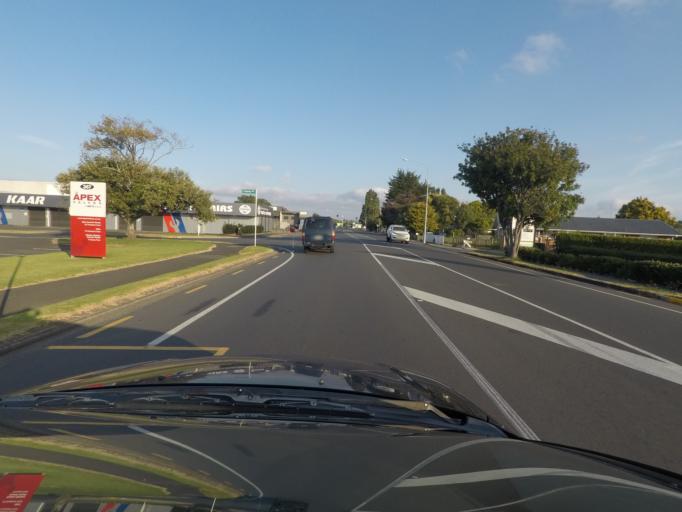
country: NZ
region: Auckland
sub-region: Auckland
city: Rosebank
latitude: -36.8832
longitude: 174.6805
